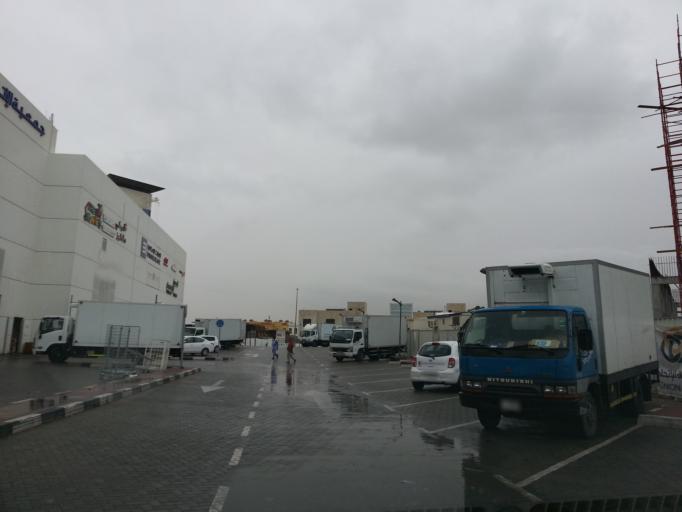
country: AE
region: Dubai
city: Dubai
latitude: 25.0983
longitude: 55.2038
